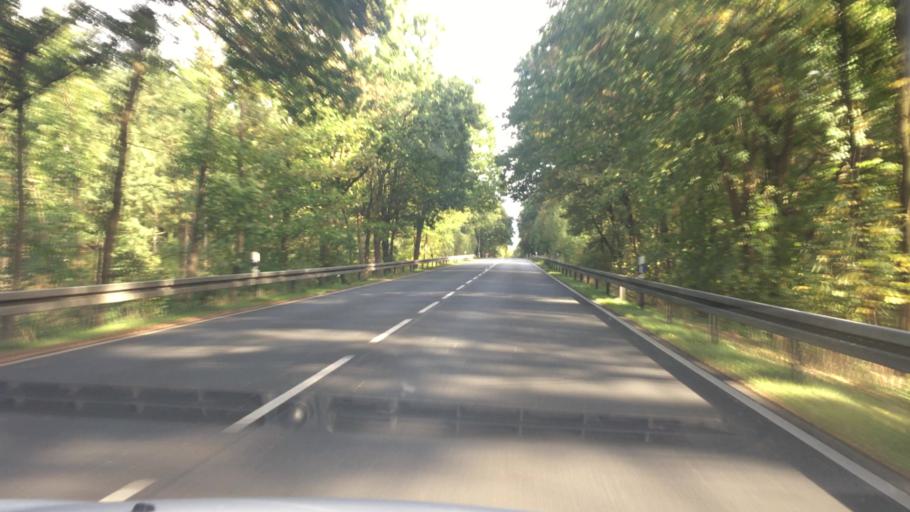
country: DE
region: Lower Saxony
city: Hemsloh
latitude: 52.6113
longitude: 8.5265
